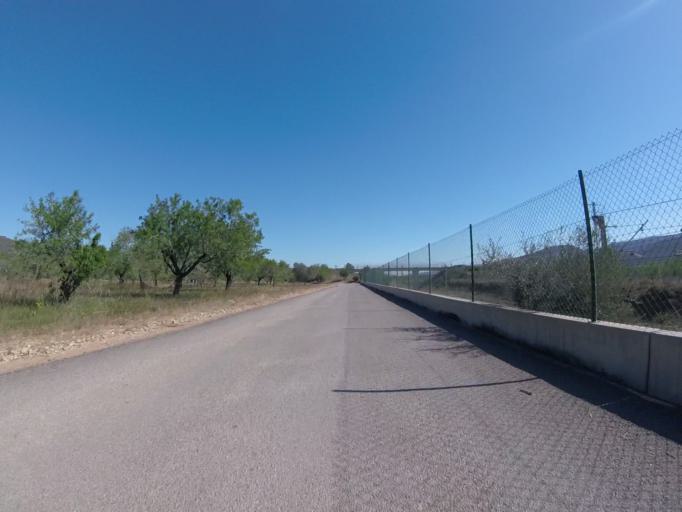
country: ES
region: Valencia
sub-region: Provincia de Castello
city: Alcala de Xivert
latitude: 40.3342
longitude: 0.2524
